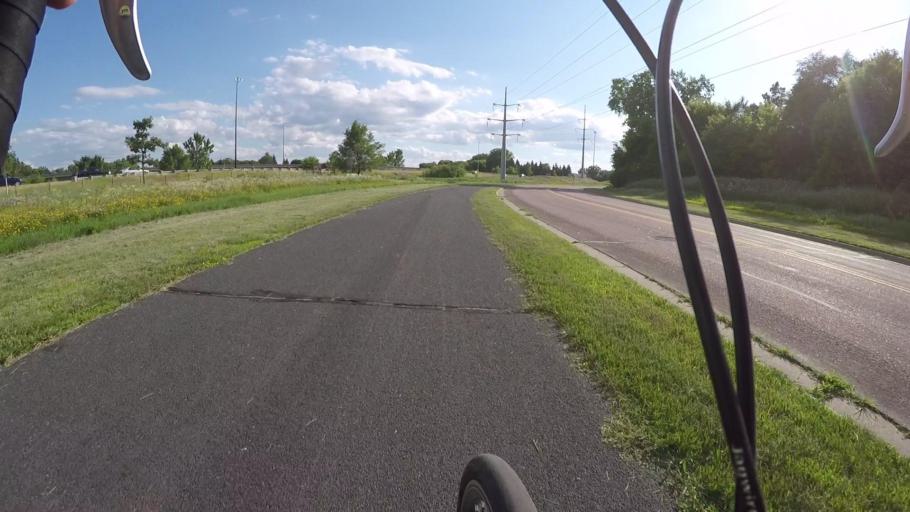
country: US
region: Minnesota
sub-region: Hennepin County
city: Eden Prairie
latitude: 44.8628
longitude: -93.4735
